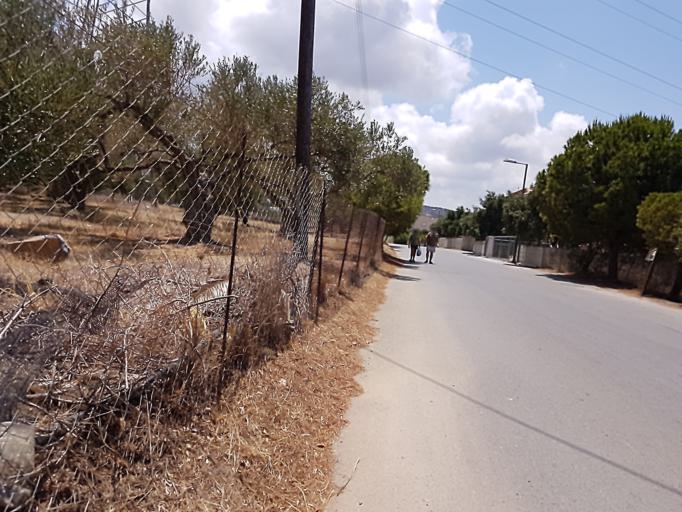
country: GR
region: Crete
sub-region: Nomos Irakleiou
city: Limin Khersonisou
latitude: 35.3146
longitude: 25.3800
